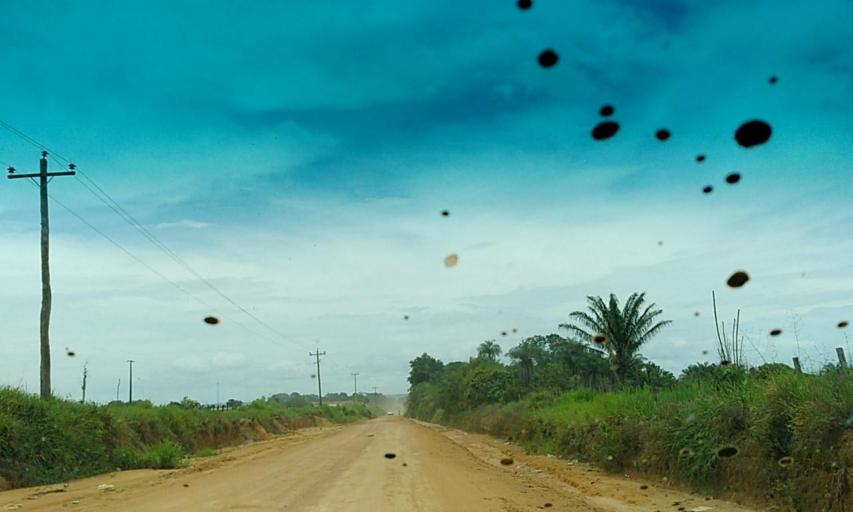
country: BR
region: Para
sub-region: Senador Jose Porfirio
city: Senador Jose Porfirio
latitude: -2.5817
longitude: -51.9309
